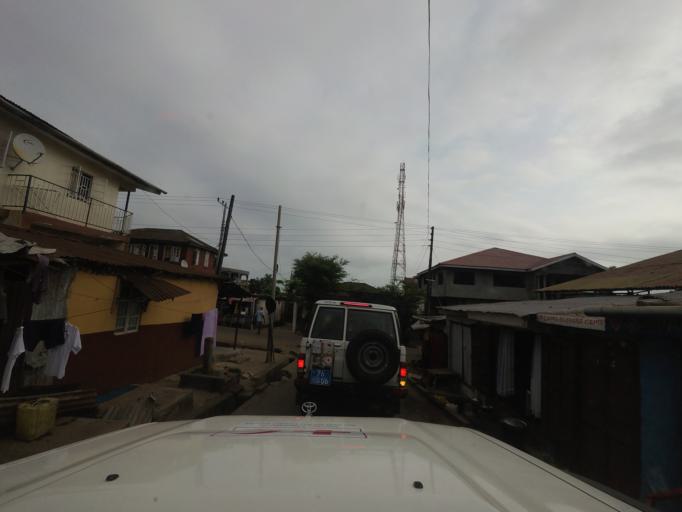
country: SL
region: Western Area
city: Freetown
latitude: 8.4829
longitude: -13.2572
